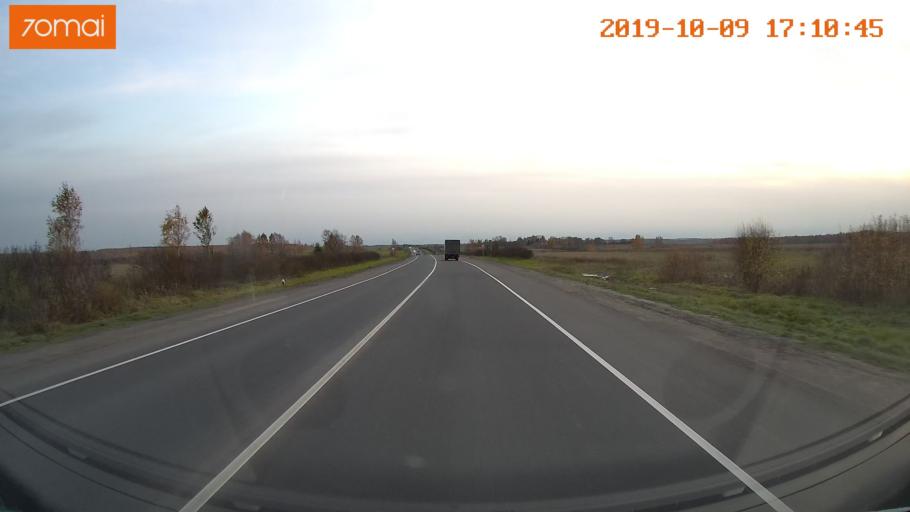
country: RU
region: Ivanovo
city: Privolzhsk
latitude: 57.3516
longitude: 41.2550
